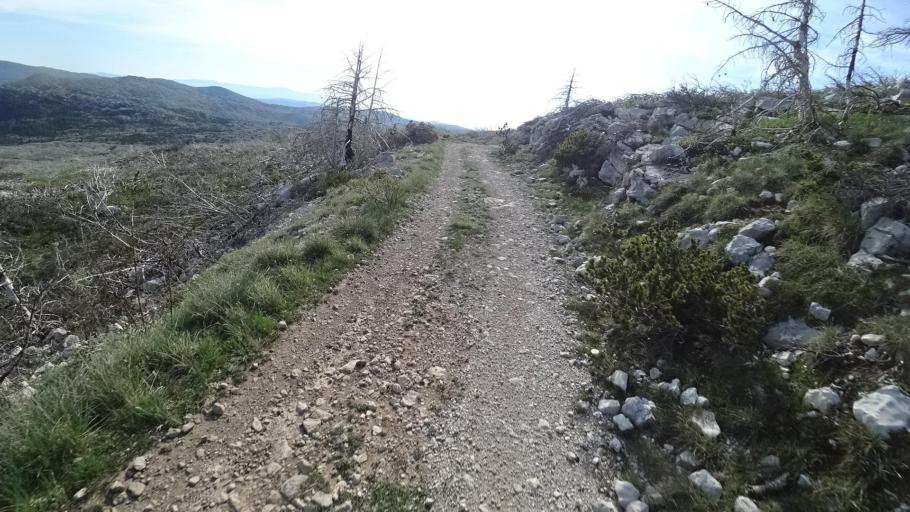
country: BA
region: Federation of Bosnia and Herzegovina
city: Kocerin
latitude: 43.5811
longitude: 17.5429
